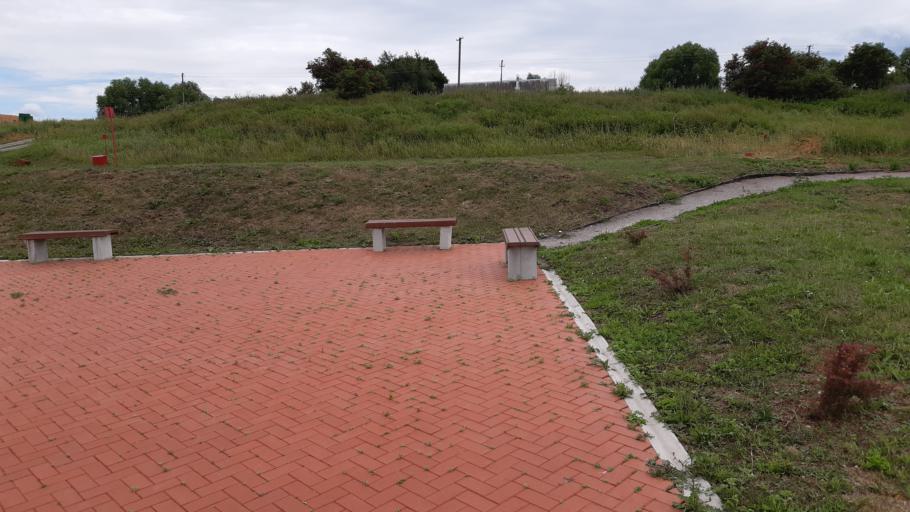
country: RU
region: Tula
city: Yepifan'
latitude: 53.6698
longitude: 38.6537
